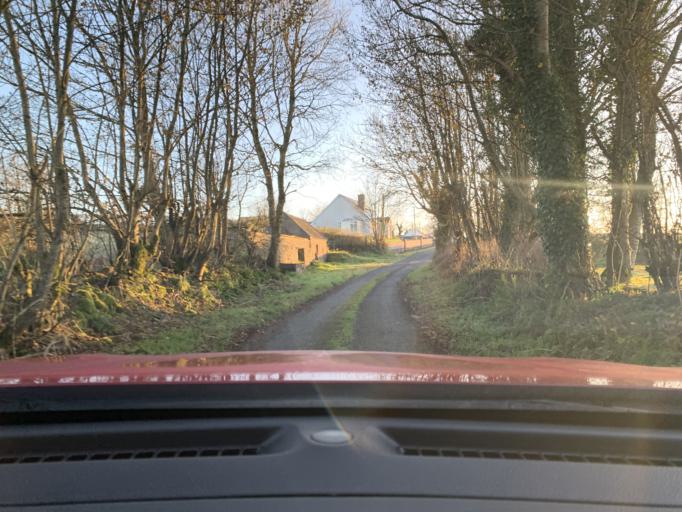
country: IE
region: Connaught
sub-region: Sligo
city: Ballymote
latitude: 54.0676
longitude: -8.5461
